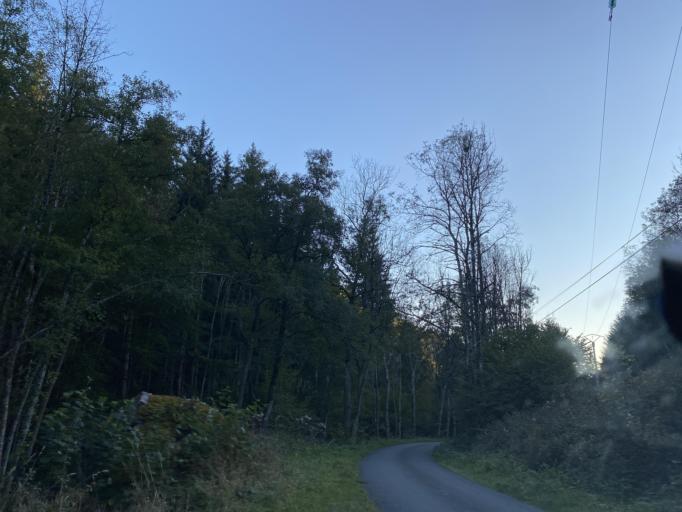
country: FR
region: Rhone-Alpes
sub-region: Departement de la Loire
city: Saint-Just-en-Chevalet
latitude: 45.9309
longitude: 3.8522
